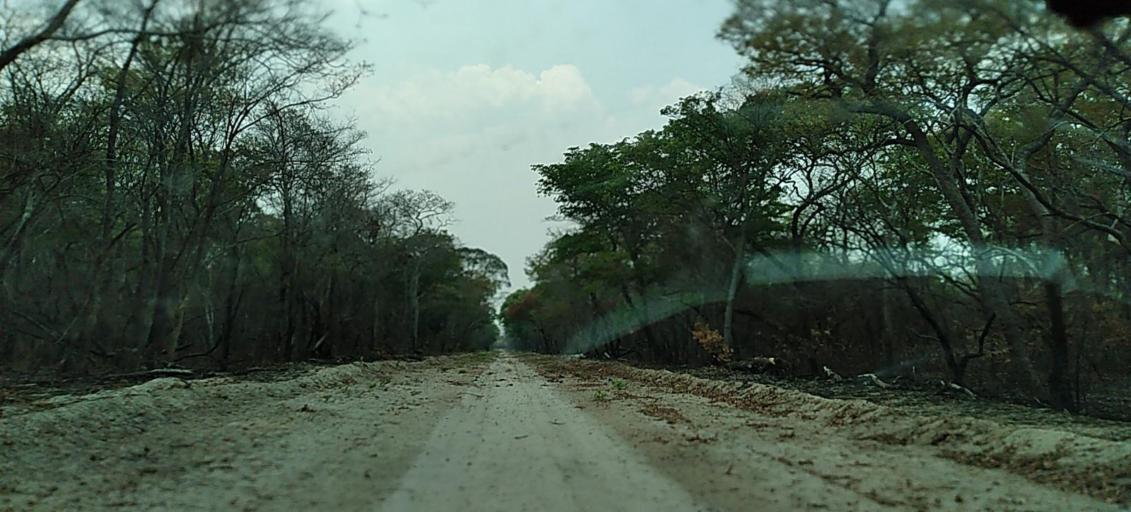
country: ZM
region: Western
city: Lukulu
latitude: -14.0124
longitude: 23.5813
